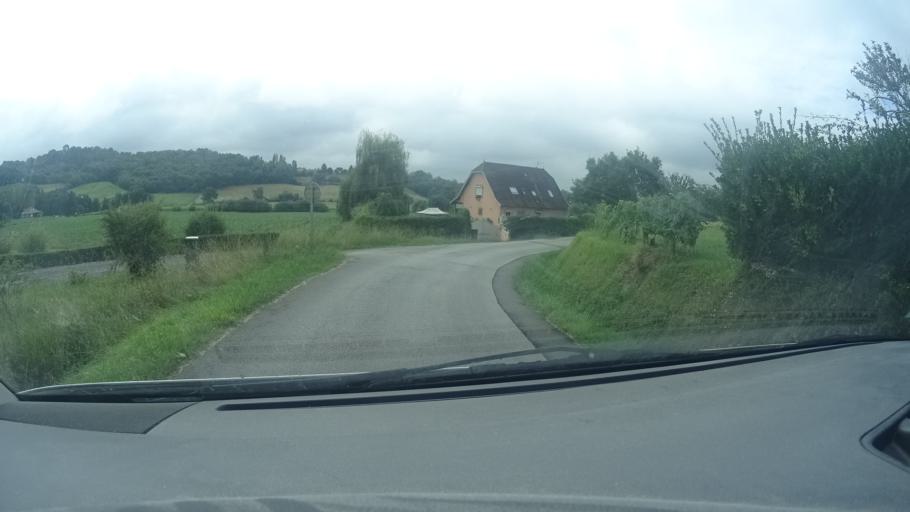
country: FR
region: Aquitaine
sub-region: Departement des Pyrenees-Atlantiques
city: Orthez
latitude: 43.4878
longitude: -0.7005
